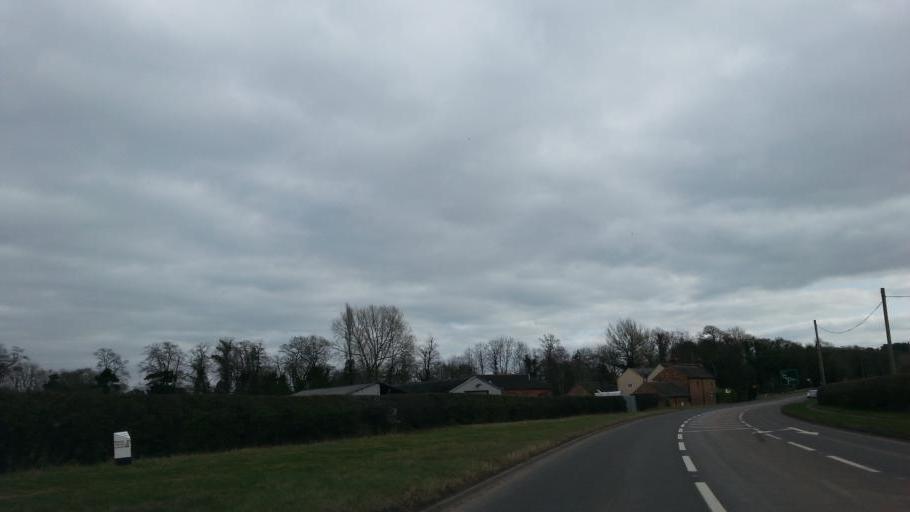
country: GB
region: England
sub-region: Staffordshire
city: Colwich
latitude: 52.7840
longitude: -1.9735
